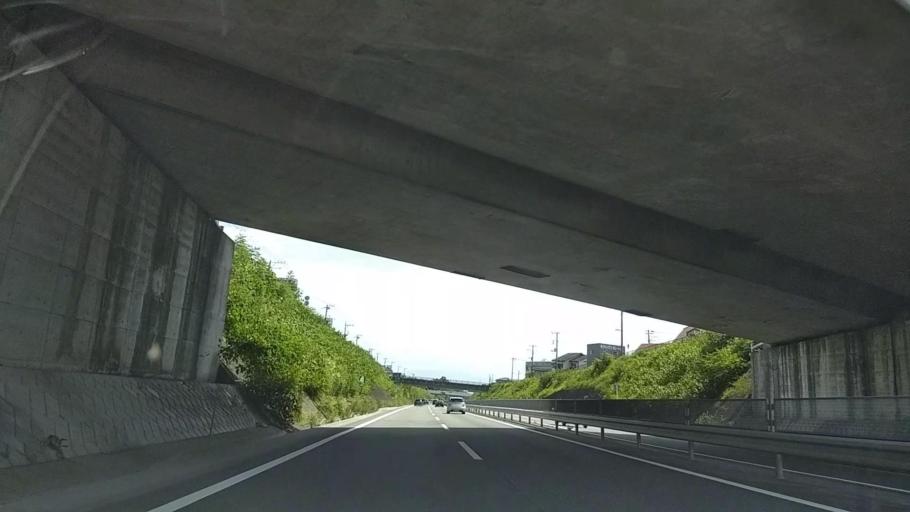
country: JP
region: Shizuoka
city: Fuji
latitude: 35.1918
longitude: 138.6720
